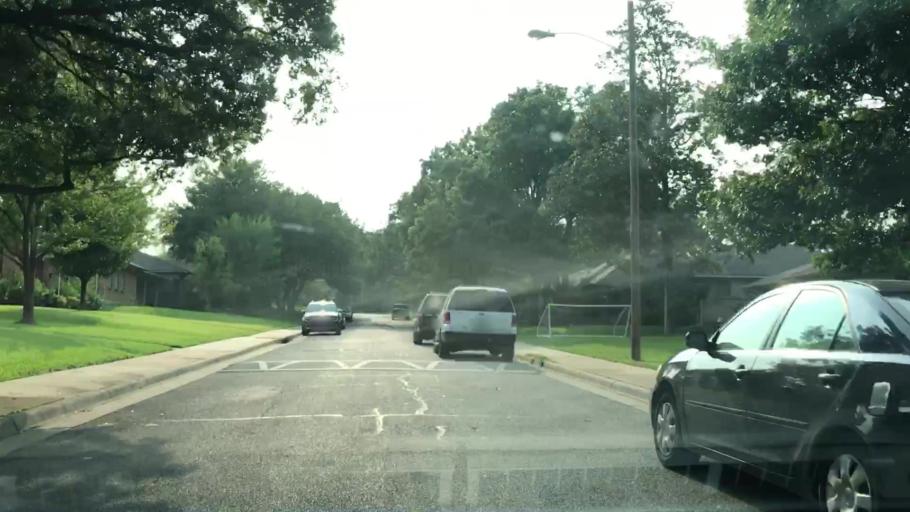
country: US
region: Texas
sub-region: Dallas County
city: Richardson
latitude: 32.9048
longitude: -96.7308
